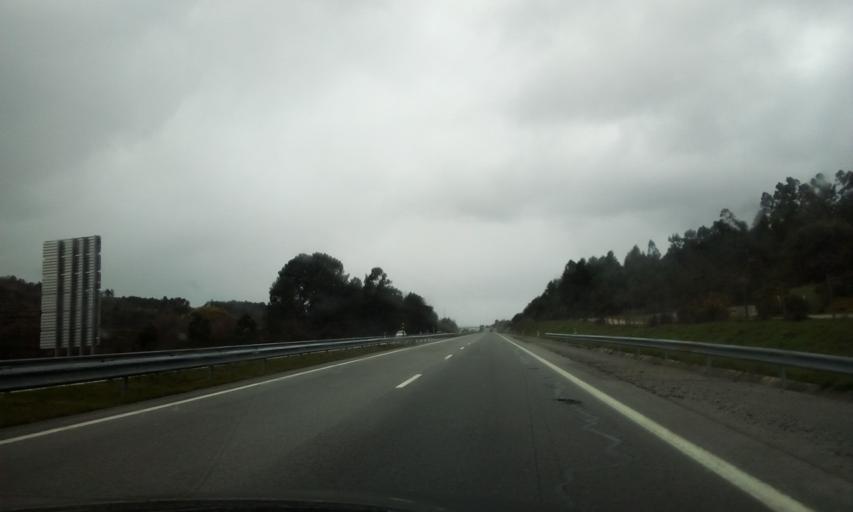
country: PT
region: Viseu
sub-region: Mangualde
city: Mangualde
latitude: 40.6138
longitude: -7.6510
